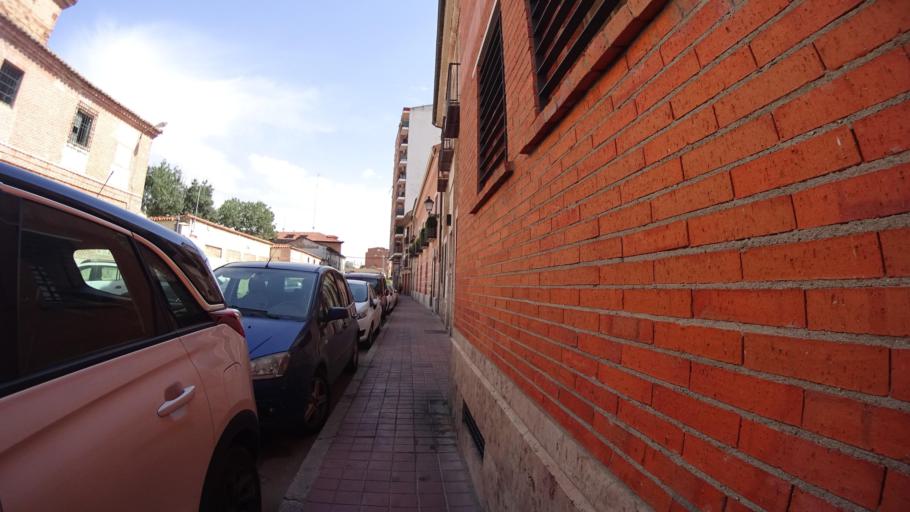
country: ES
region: Madrid
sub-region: Provincia de Madrid
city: Alcala de Henares
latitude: 40.4782
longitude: -3.3674
